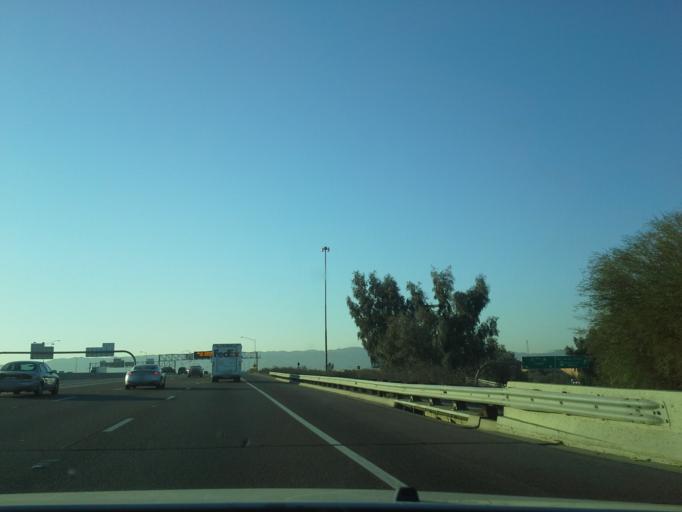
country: US
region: Arizona
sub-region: Maricopa County
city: Phoenix
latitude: 33.4474
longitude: -112.0376
